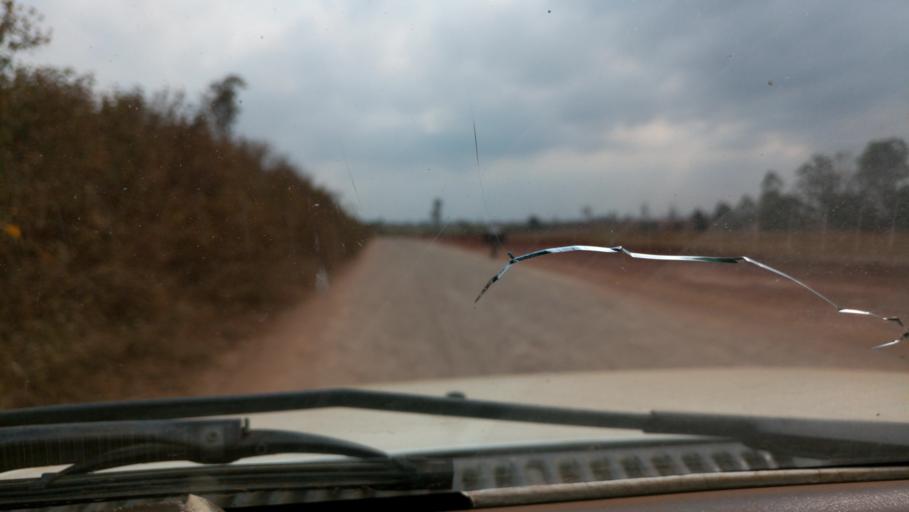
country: KE
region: Nairobi Area
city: Thika
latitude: -1.0198
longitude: 37.2037
